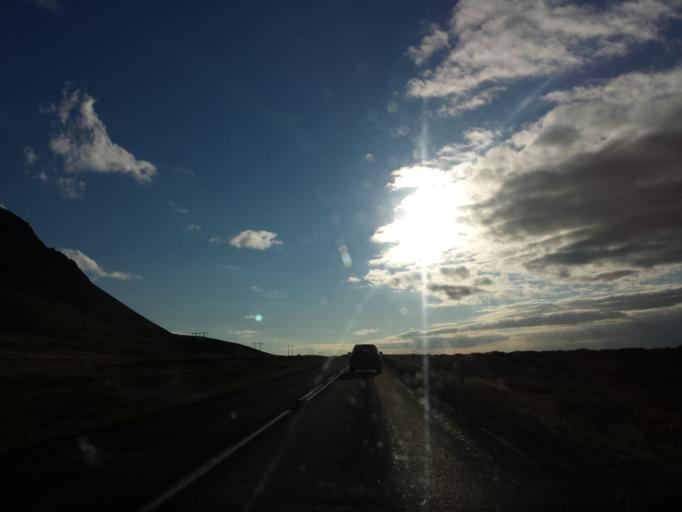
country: IS
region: West
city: Borgarnes
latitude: 64.5043
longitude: -21.9263
